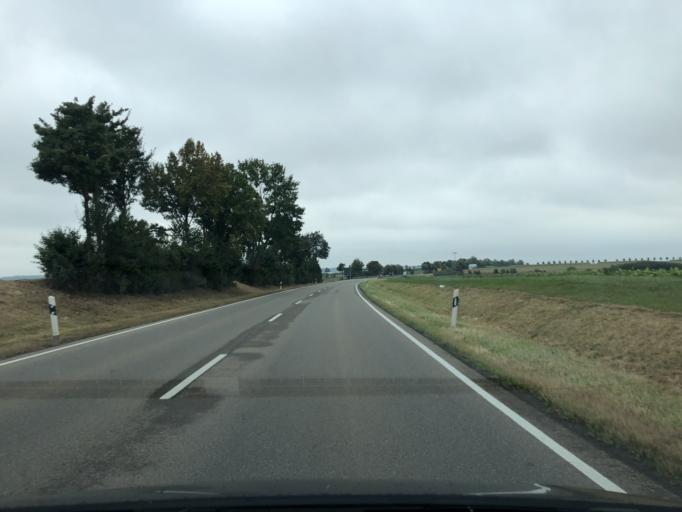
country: DE
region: Baden-Wuerttemberg
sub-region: Regierungsbezirk Stuttgart
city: Bondorf
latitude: 48.5379
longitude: 8.8426
